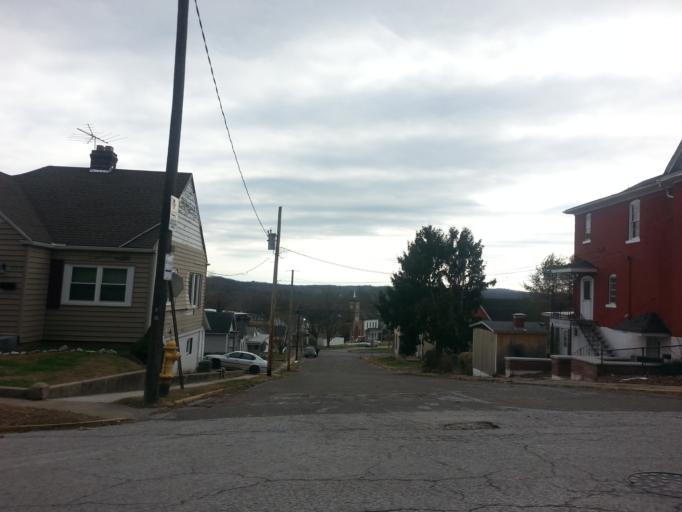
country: US
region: Missouri
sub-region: Marion County
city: Hannibal
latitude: 39.7035
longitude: -91.3734
